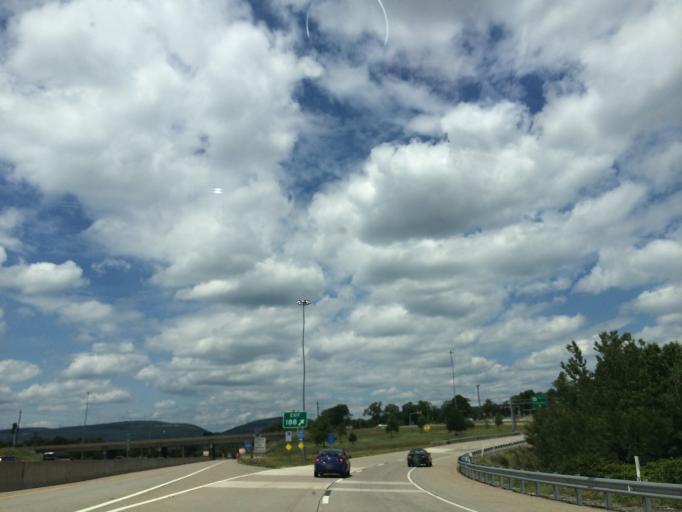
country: US
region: Pennsylvania
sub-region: Lackawanna County
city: Dunmore
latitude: 41.4300
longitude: -75.6196
